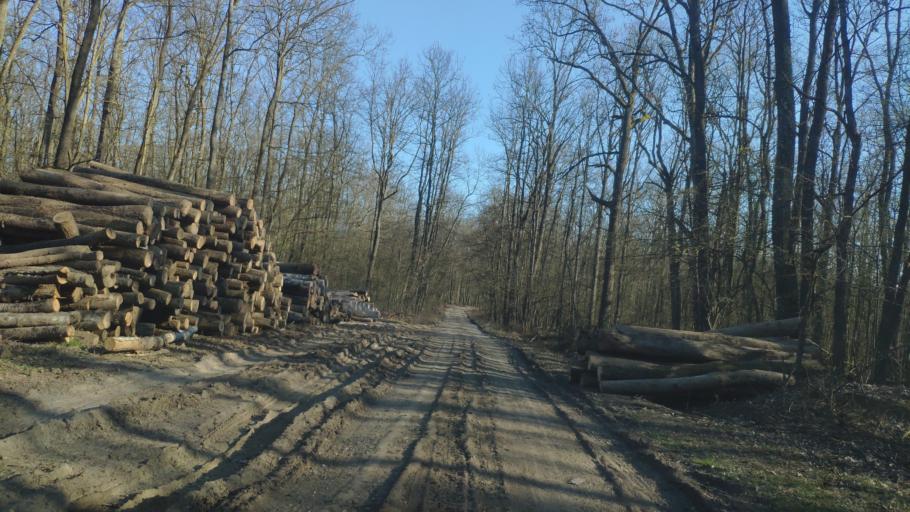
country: SK
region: Banskobystricky
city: Revuca
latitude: 48.5042
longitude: 20.2886
